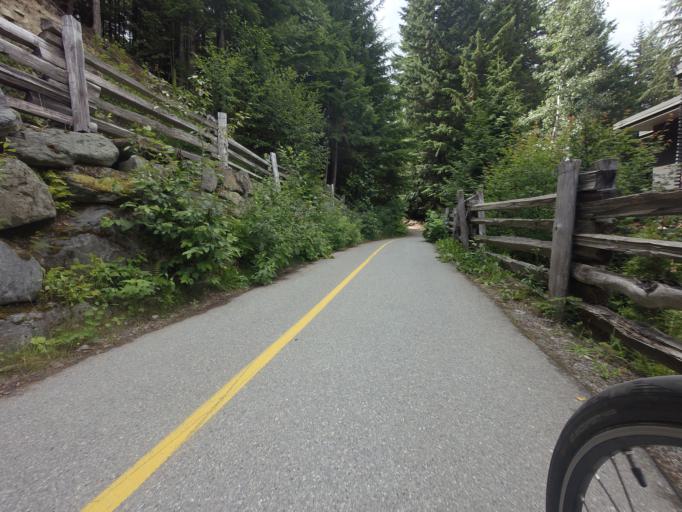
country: CA
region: British Columbia
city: Whistler
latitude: 50.1057
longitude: -122.9839
